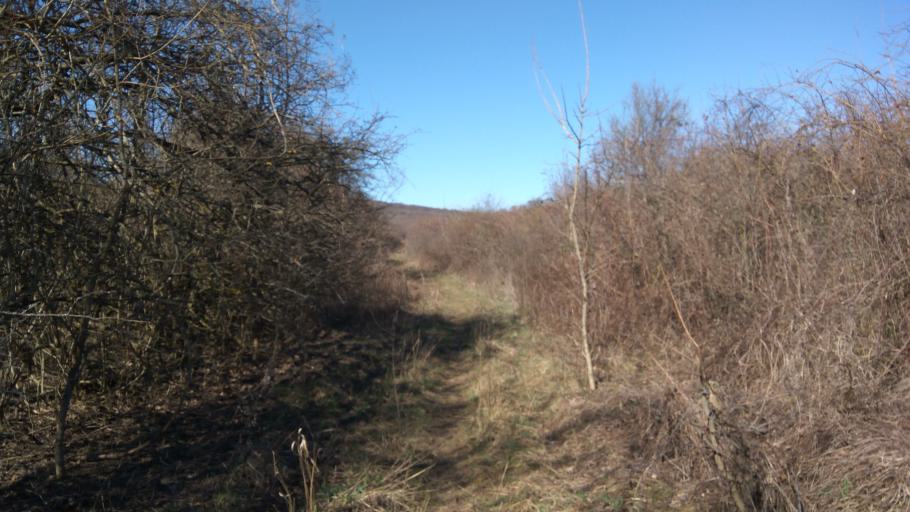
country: HU
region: Pest
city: Nagykovacsi
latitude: 47.6407
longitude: 18.9974
